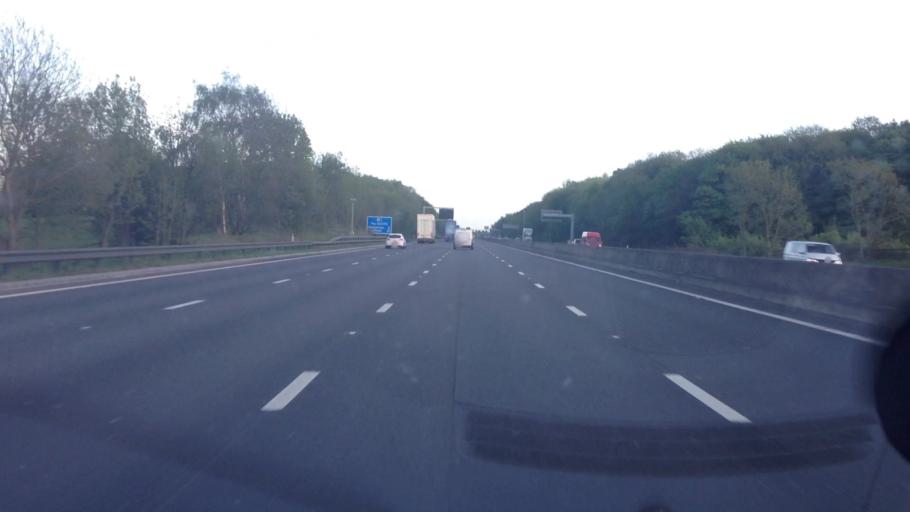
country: GB
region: England
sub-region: Sheffield
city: Chapletown
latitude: 53.4708
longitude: -1.4550
